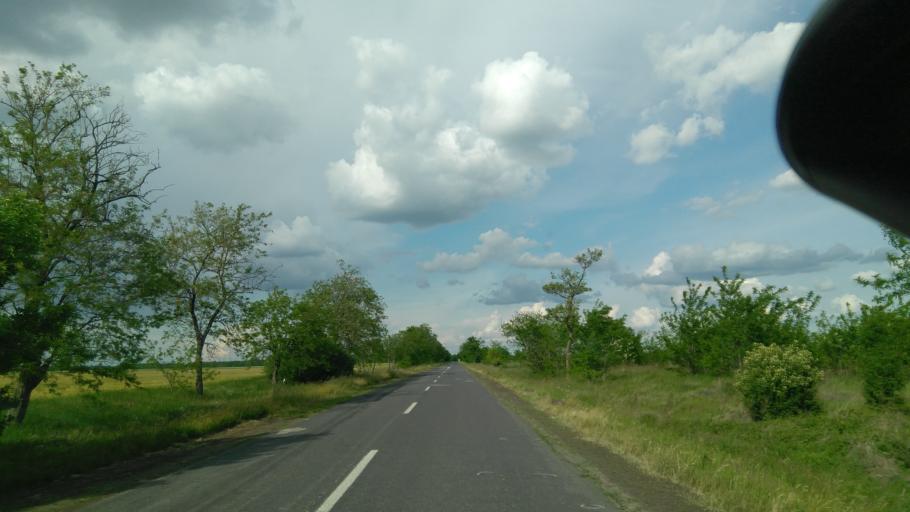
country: HU
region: Bekes
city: Battonya
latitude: 46.3117
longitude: 21.0707
